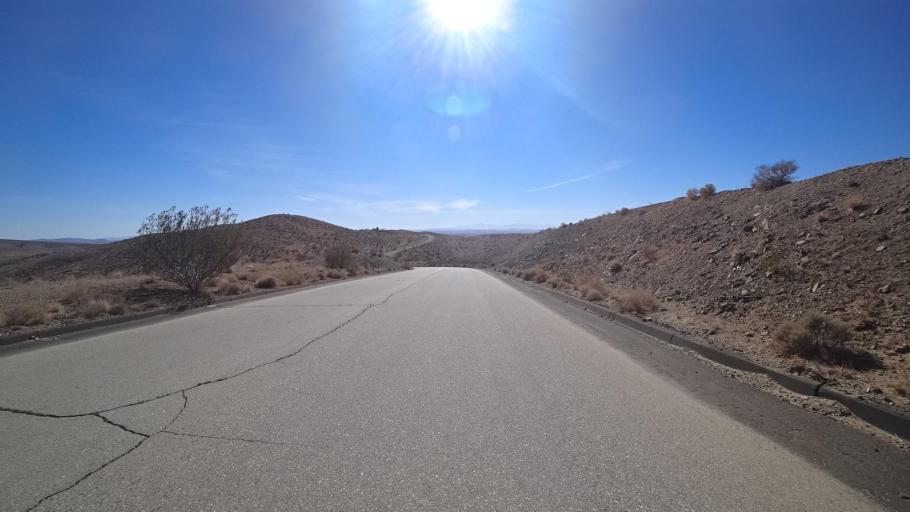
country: US
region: California
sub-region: Kern County
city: Ridgecrest
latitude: 35.3537
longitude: -117.6335
